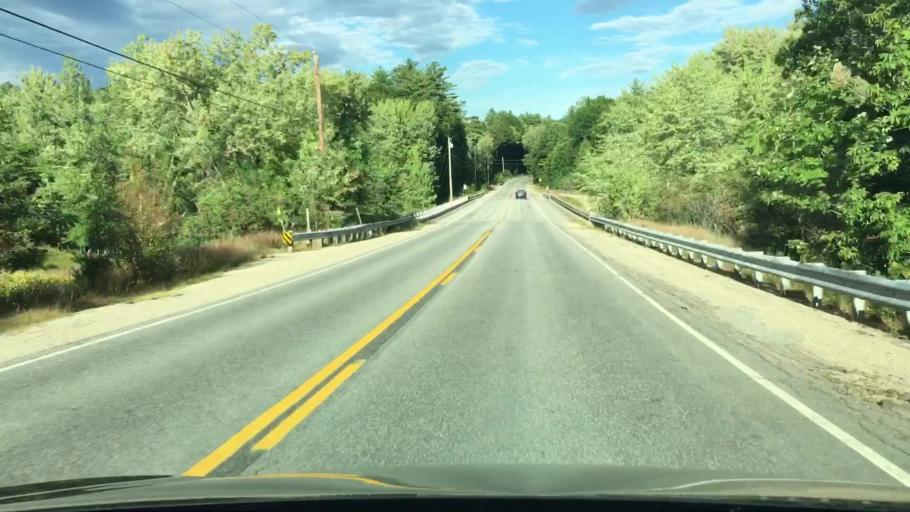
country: US
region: Maine
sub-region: Oxford County
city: Fryeburg
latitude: 44.0288
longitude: -70.9216
